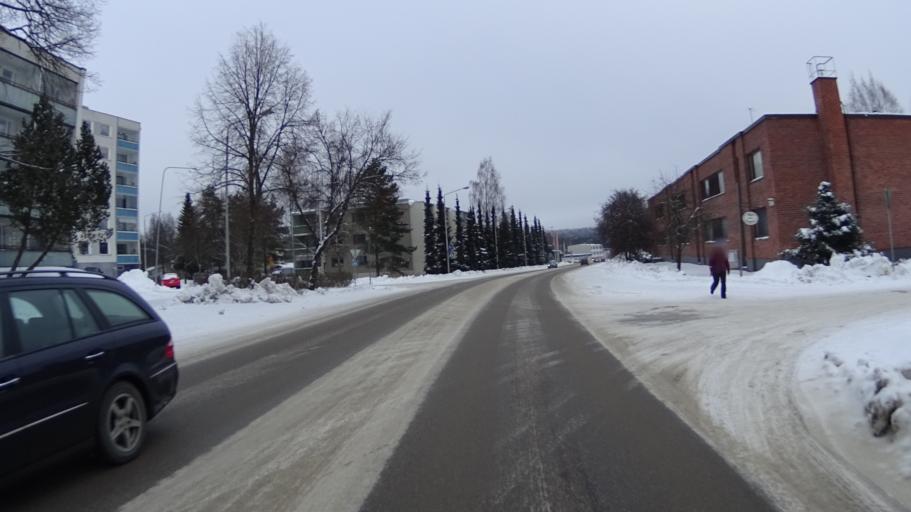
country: FI
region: Uusimaa
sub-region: Helsinki
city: Karkkila
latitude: 60.5344
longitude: 24.2210
